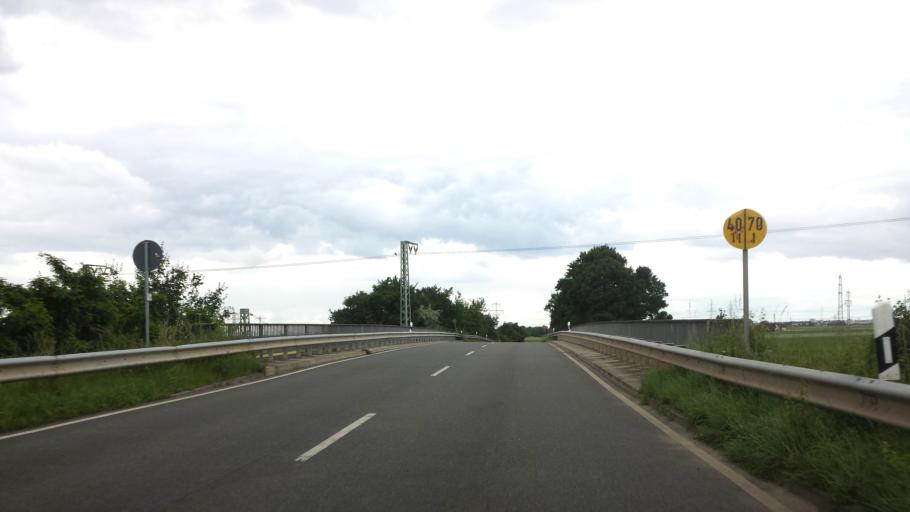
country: DE
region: Baden-Wuerttemberg
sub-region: Karlsruhe Region
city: Edingen-Neckarhausen
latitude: 49.4282
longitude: 8.5999
